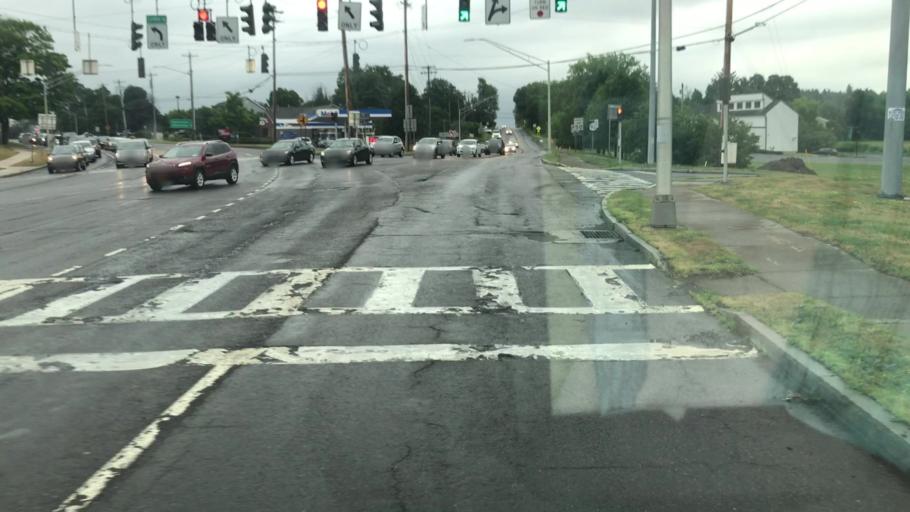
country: US
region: New York
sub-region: Onondaga County
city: Fayetteville
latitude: 43.0283
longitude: -76.0453
